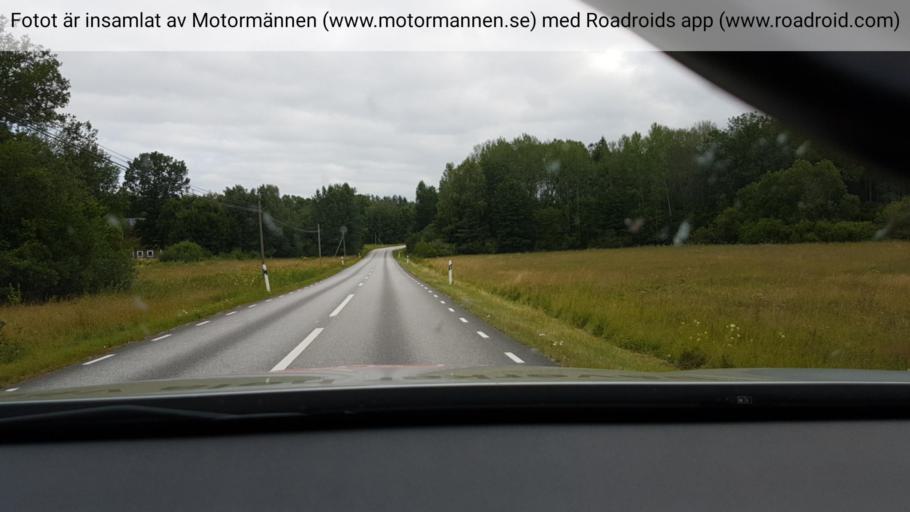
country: SE
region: Stockholm
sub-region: Norrtalje Kommun
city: Skanninge
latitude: 59.8523
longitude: 18.4459
